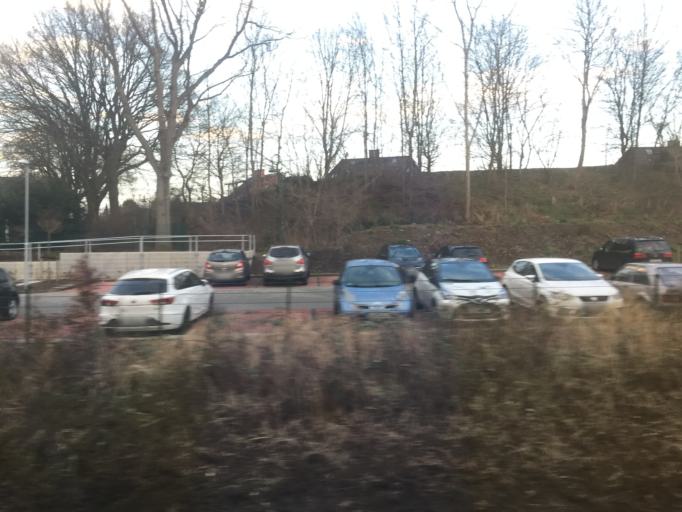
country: DE
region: Schleswig-Holstein
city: Prisdorf
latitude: 53.6752
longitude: 9.7603
